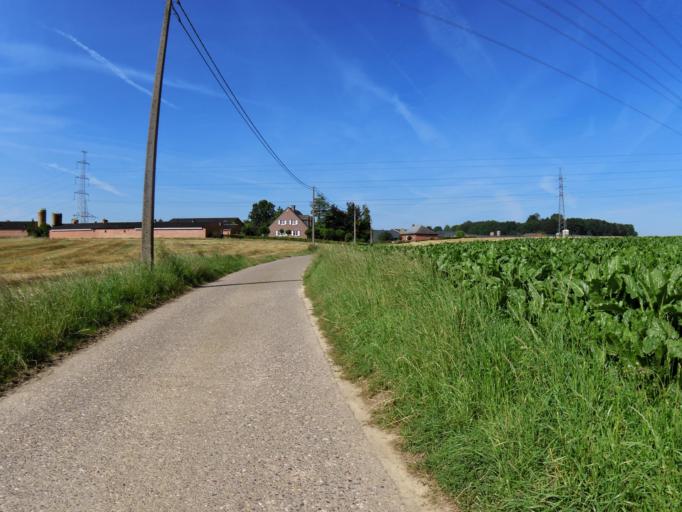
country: BE
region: Flanders
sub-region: Provincie Limburg
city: Riemst
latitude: 50.8050
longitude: 5.5612
